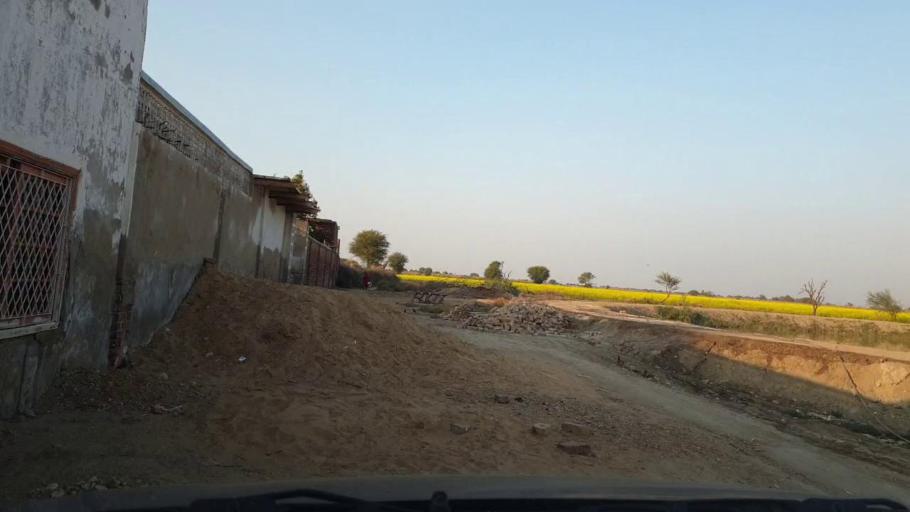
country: PK
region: Sindh
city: Jhol
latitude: 25.9345
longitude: 68.9333
